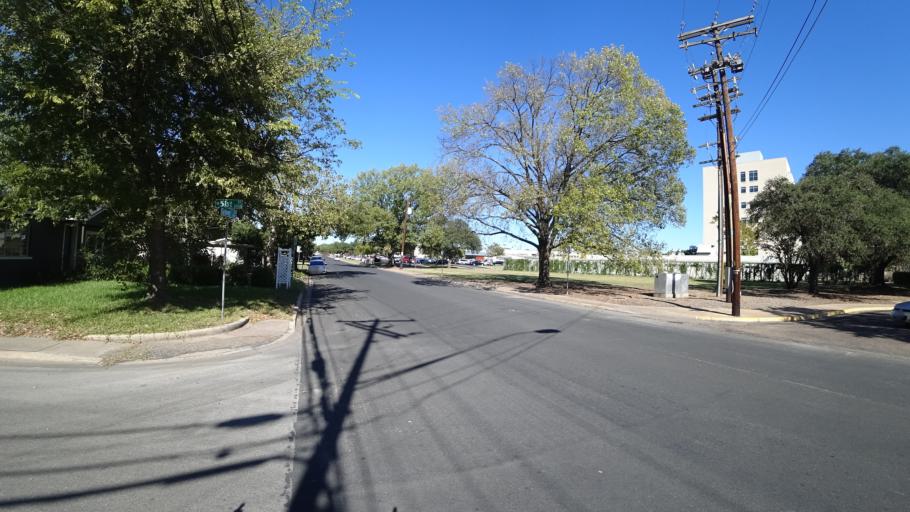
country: US
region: Texas
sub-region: Travis County
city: Austin
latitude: 30.3206
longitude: -97.7358
